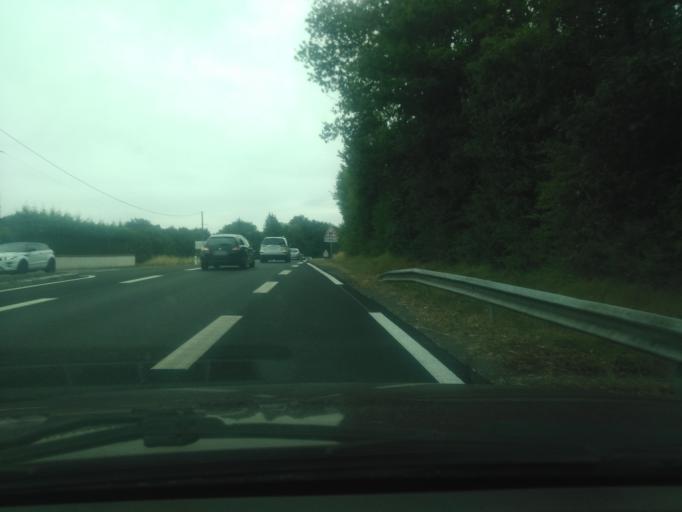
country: FR
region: Poitou-Charentes
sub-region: Departement de la Vienne
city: Chauvigny
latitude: 46.5685
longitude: 0.6592
